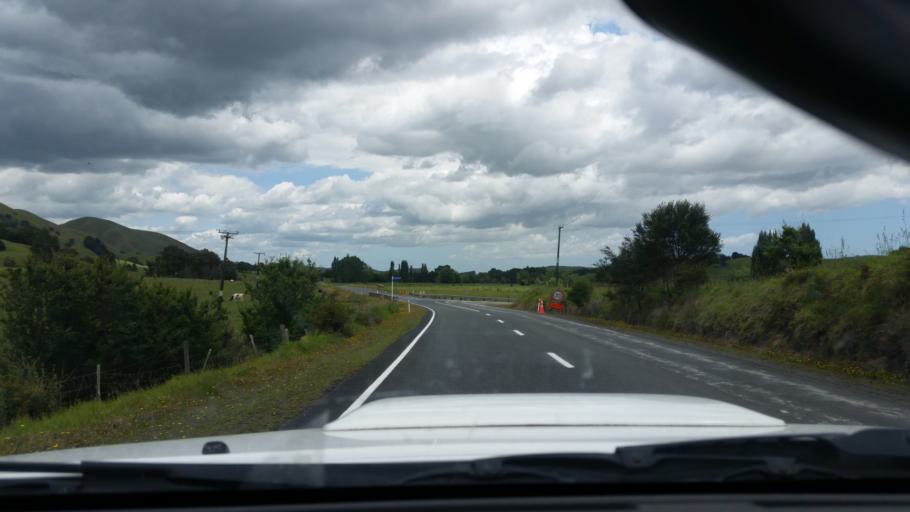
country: NZ
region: Northland
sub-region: Kaipara District
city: Dargaville
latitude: -35.8005
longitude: 173.9178
